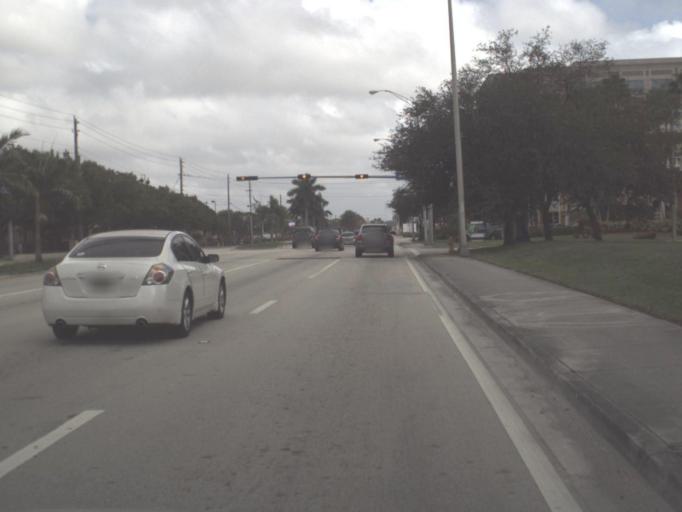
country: US
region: Florida
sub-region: Miami-Dade County
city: Doral
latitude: 25.8097
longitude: -80.3348
